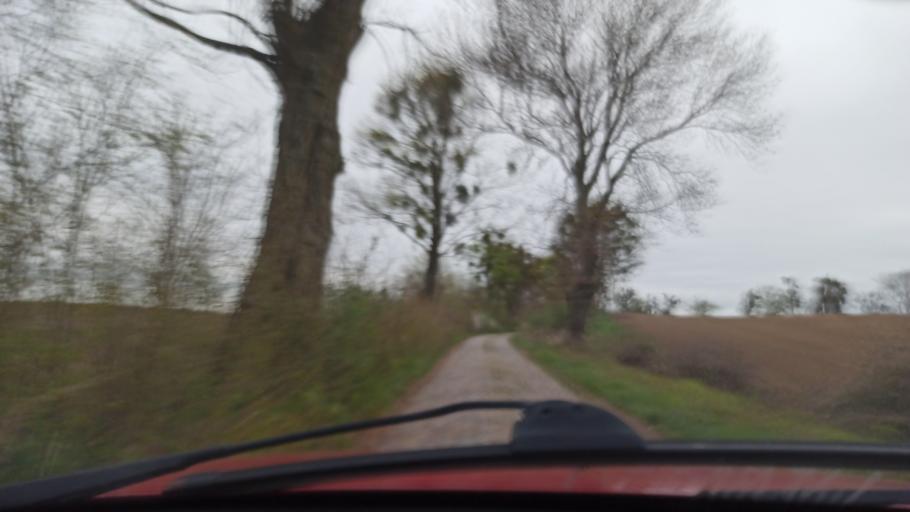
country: PL
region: Kujawsko-Pomorskie
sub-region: Powiat grudziadzki
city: Lasin
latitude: 53.5742
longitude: 19.0878
